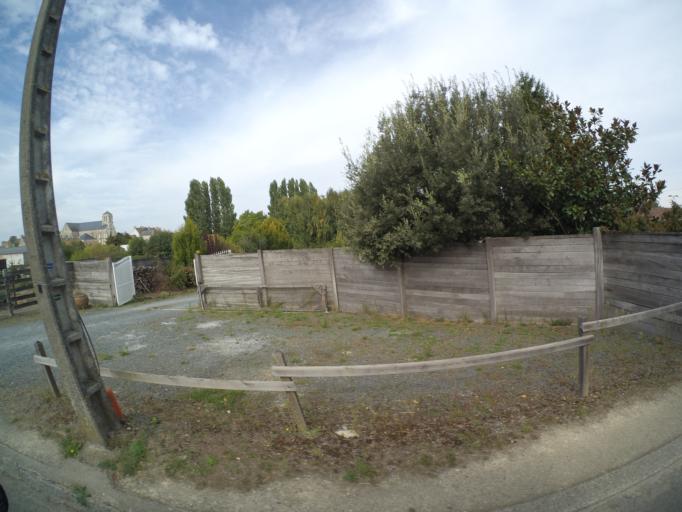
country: FR
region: Pays de la Loire
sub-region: Departement de Maine-et-Loire
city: Vihiers
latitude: 47.2125
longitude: -0.5914
